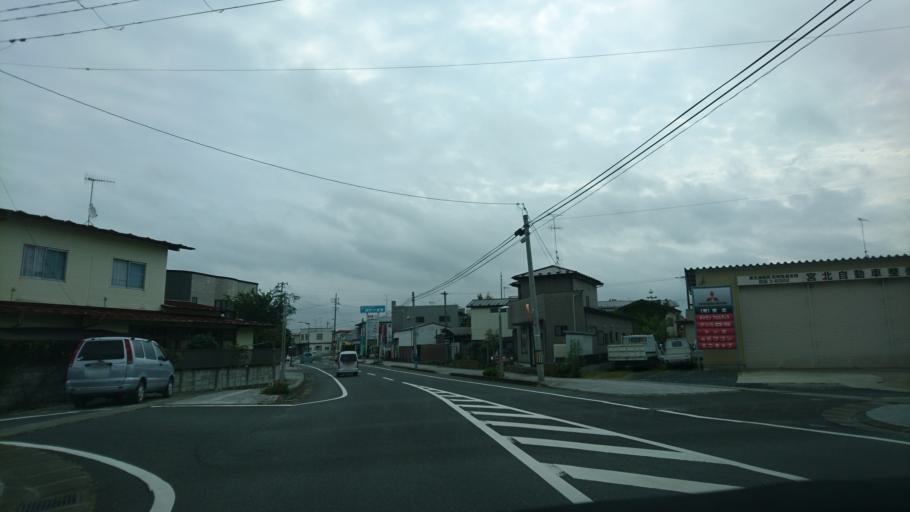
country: JP
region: Iwate
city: Ichinoseki
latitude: 38.7711
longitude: 141.1331
